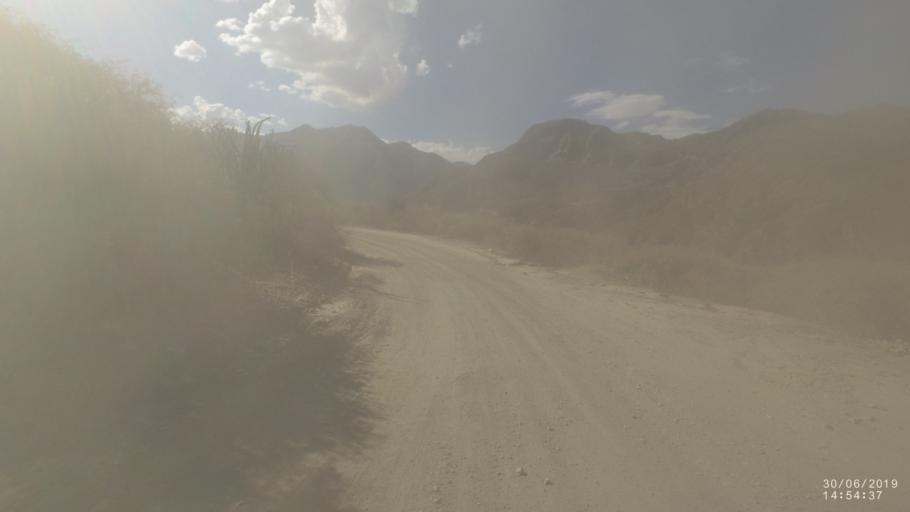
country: BO
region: Cochabamba
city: Irpa Irpa
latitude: -17.7578
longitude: -66.3504
